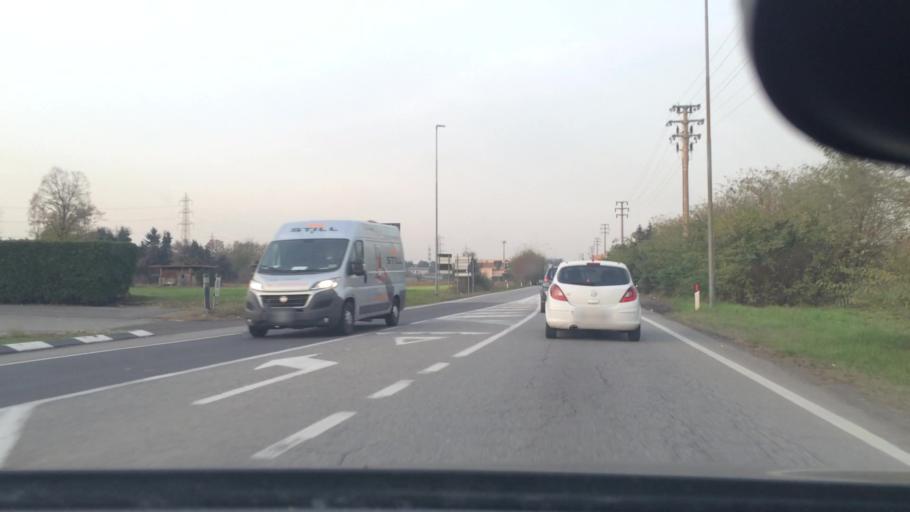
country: IT
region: Lombardy
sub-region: Provincia di Varese
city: Origgio
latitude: 45.6127
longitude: 9.0204
